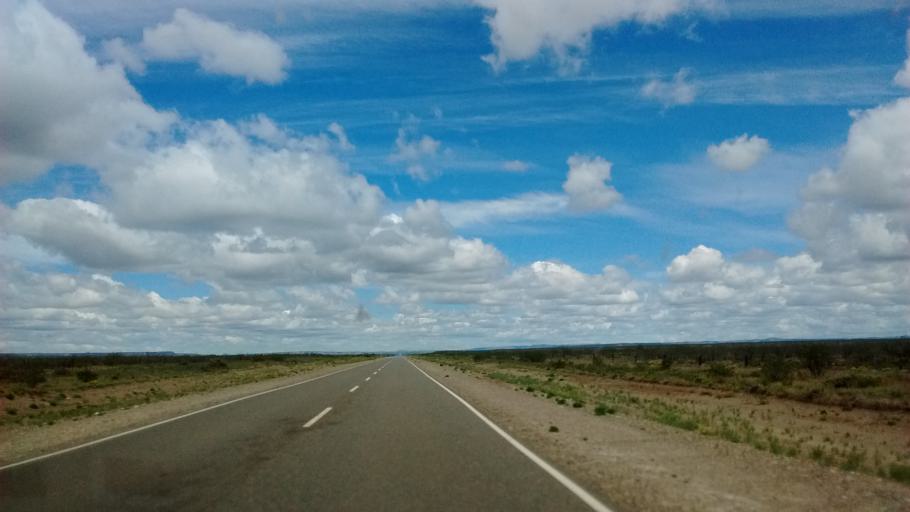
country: AR
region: Neuquen
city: Piedra del Aguila
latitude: -39.8195
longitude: -69.7332
